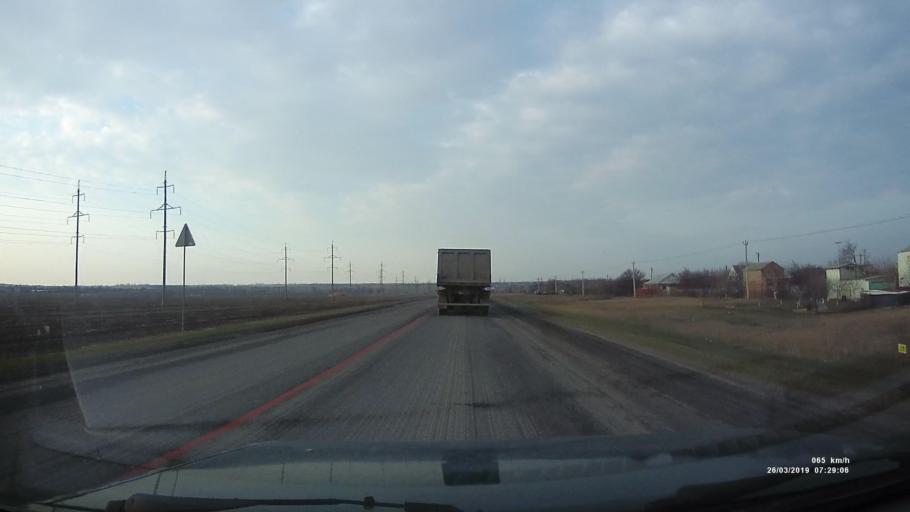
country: RU
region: Rostov
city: Novobessergenovka
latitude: 47.2482
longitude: 38.8192
